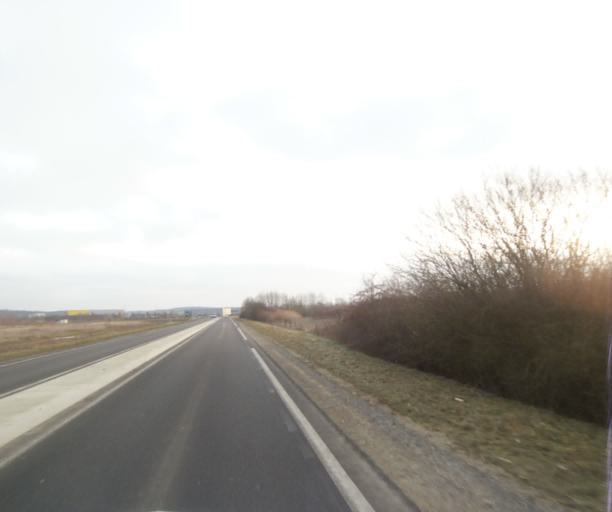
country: FR
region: Champagne-Ardenne
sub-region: Departement de la Haute-Marne
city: Saint-Dizier
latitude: 48.6495
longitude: 4.9477
